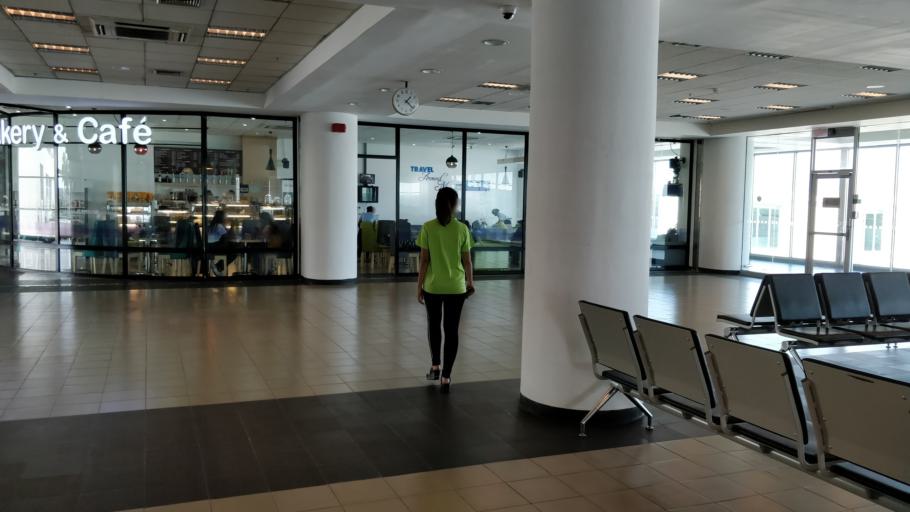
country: MM
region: Sagain
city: Sagaing
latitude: 21.7050
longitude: 95.9707
